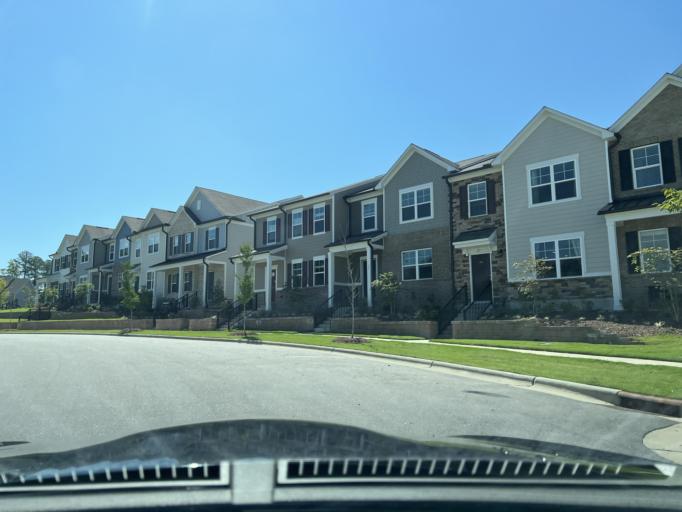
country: US
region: North Carolina
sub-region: Wake County
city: Morrisville
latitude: 35.8816
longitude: -78.8573
